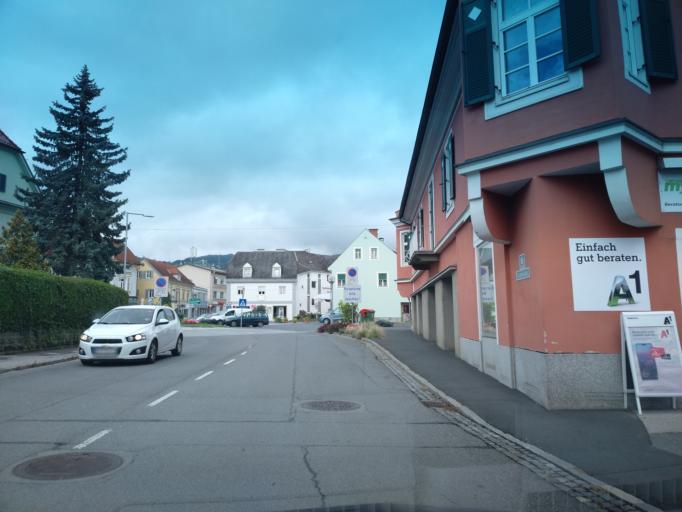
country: AT
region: Styria
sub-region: Politischer Bezirk Deutschlandsberg
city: Deutschlandsberg
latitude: 46.8153
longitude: 15.2170
